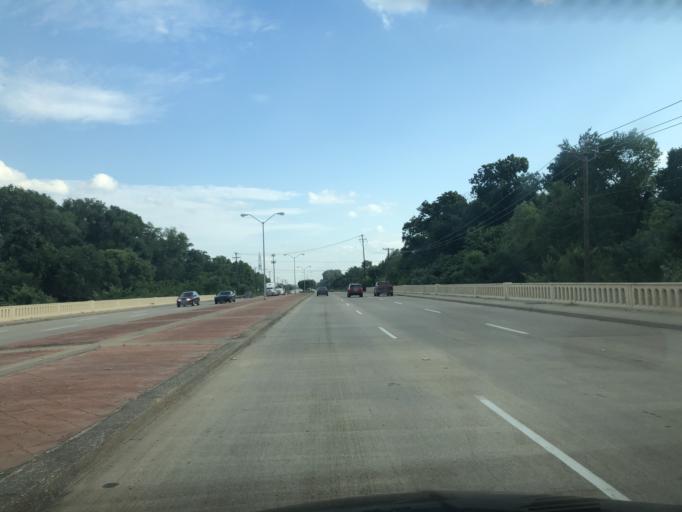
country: US
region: Texas
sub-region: Dallas County
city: Grand Prairie
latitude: 32.7893
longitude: -96.9947
